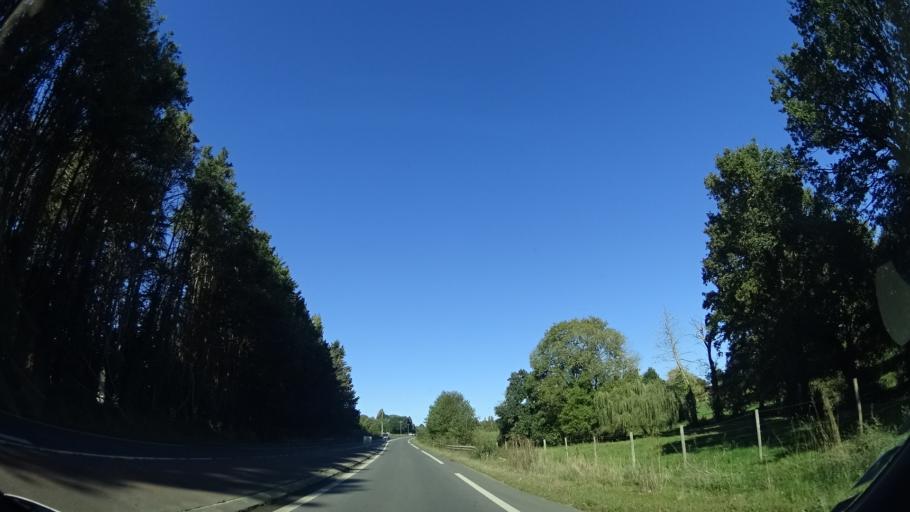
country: FR
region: Brittany
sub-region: Departement d'Ille-et-Vilaine
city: Melesse
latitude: 48.1852
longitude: -1.6937
